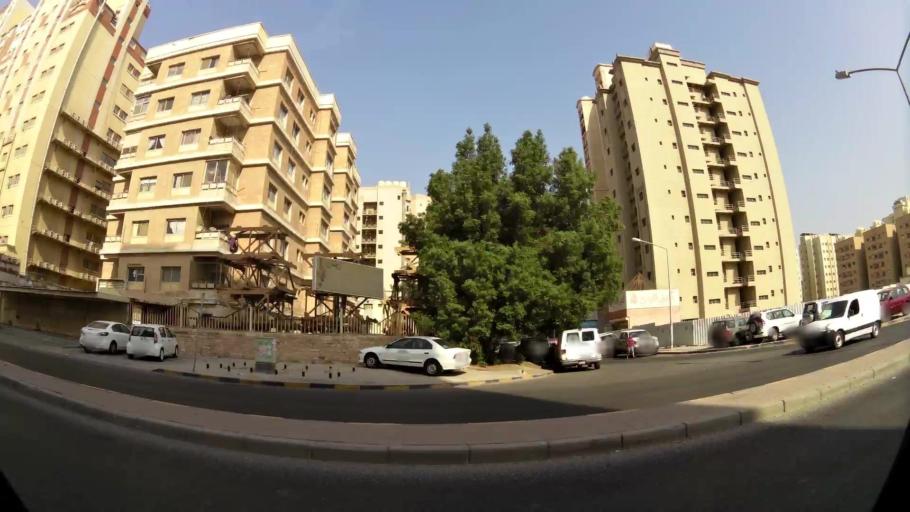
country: KW
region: Muhafazat Hawalli
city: As Salimiyah
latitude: 29.3250
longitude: 48.0582
